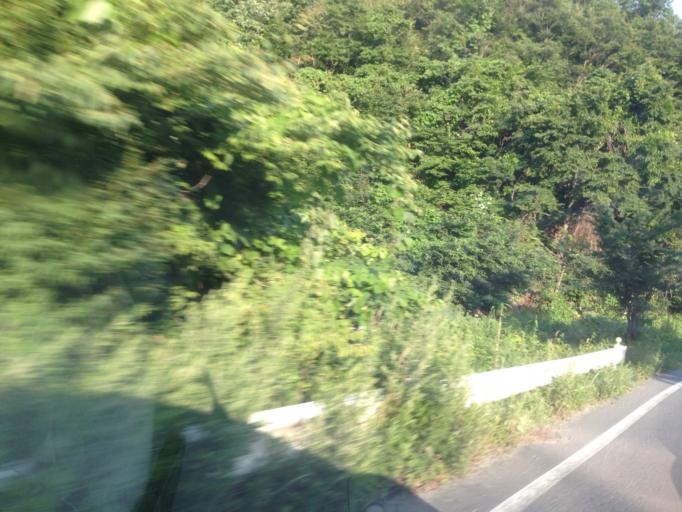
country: JP
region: Iwate
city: Otsuchi
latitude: 39.3953
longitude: 141.8633
